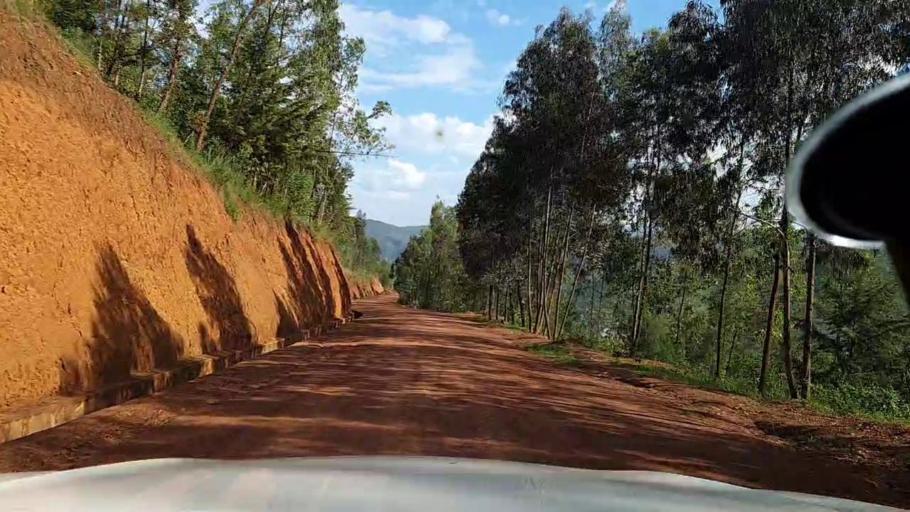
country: RW
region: Kigali
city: Kigali
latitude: -1.8386
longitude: 29.8549
